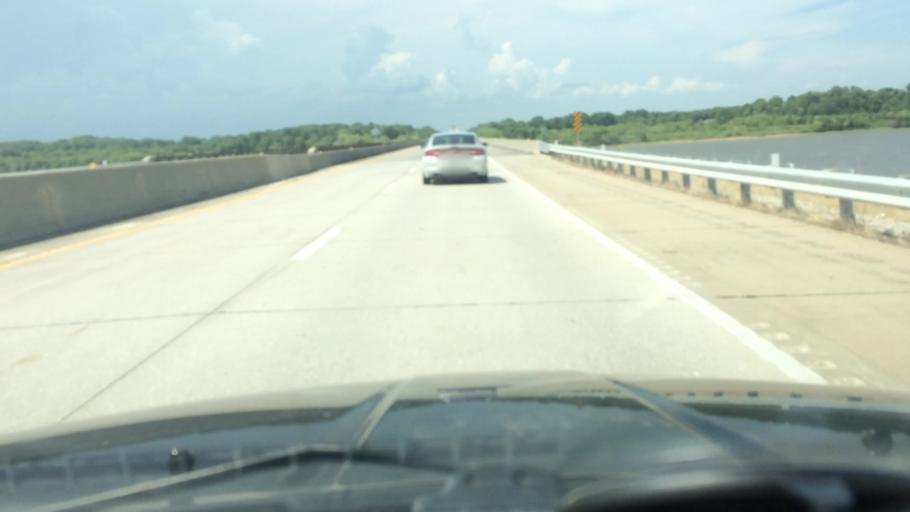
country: US
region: Missouri
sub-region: Henry County
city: Clinton
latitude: 38.2841
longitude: -93.7594
